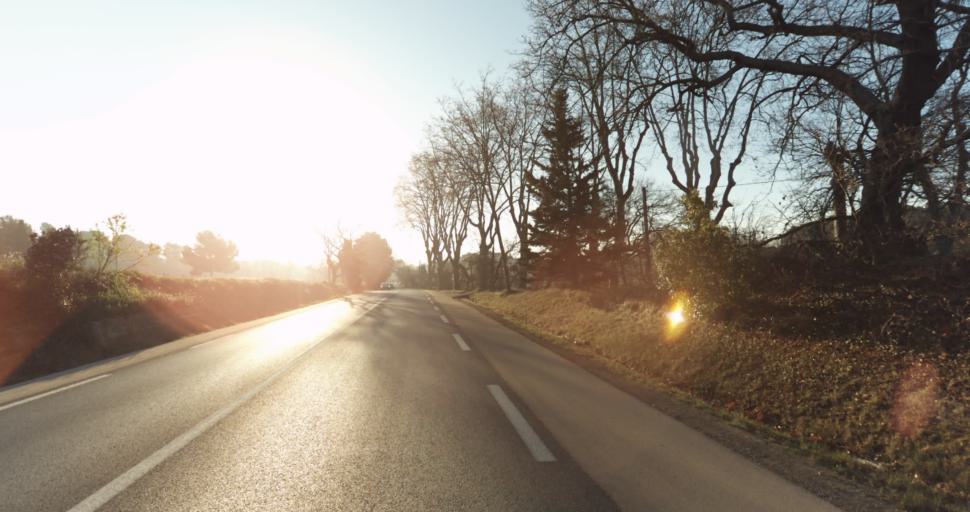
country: FR
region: Provence-Alpes-Cote d'Azur
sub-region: Departement des Bouches-du-Rhone
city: Eguilles
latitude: 43.5364
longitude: 5.3878
